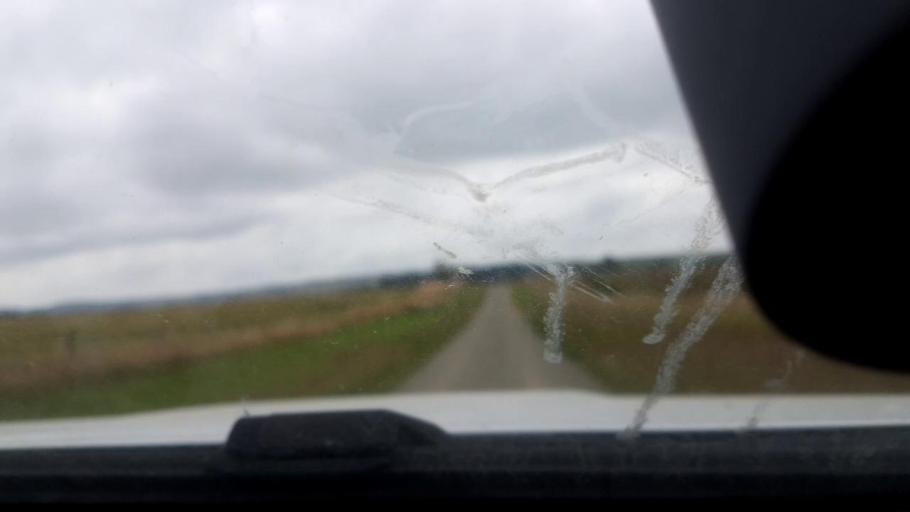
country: NZ
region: Canterbury
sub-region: Timaru District
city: Pleasant Point
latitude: -44.2290
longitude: 171.1658
